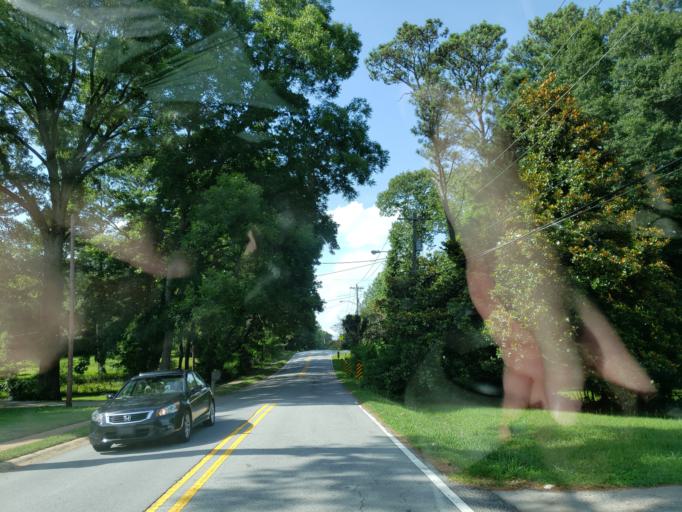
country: US
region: Georgia
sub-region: Cobb County
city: Mableton
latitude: 33.8614
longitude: -84.5689
